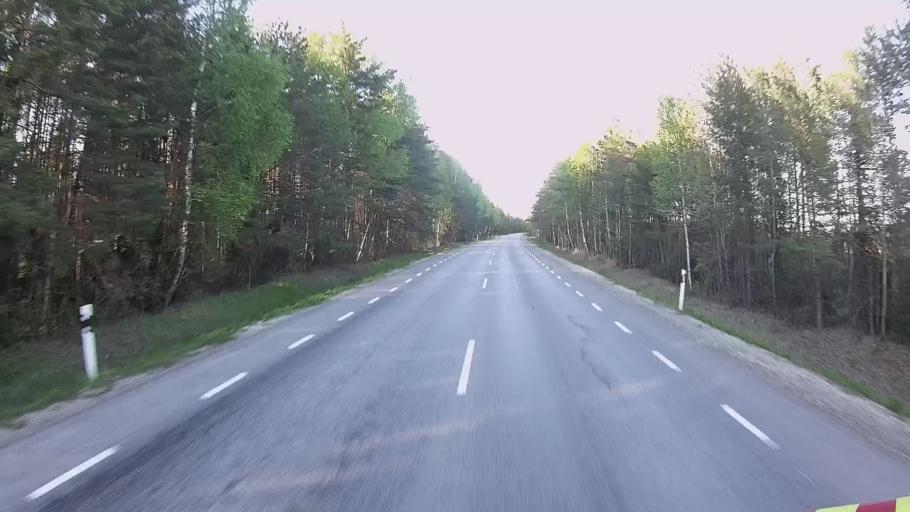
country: EE
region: Viljandimaa
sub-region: Viiratsi vald
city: Viiratsi
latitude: 58.4749
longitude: 25.7872
